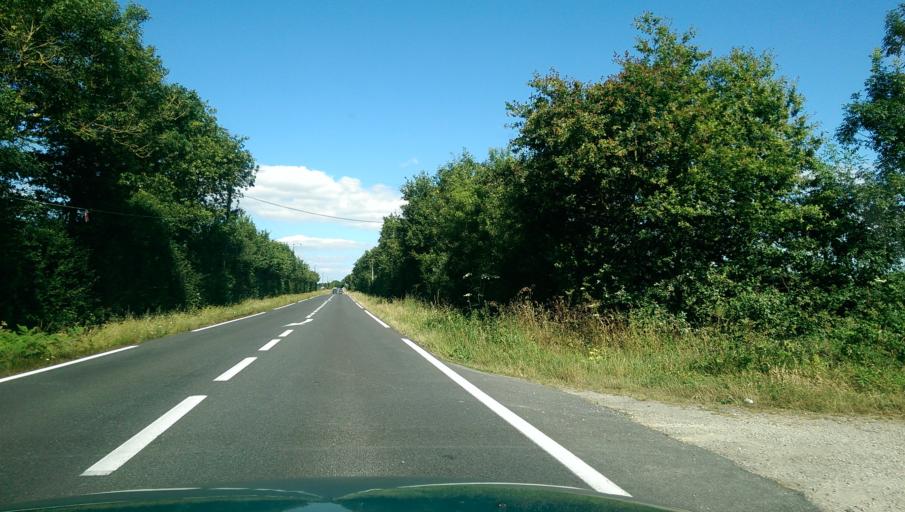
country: FR
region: Pays de la Loire
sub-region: Departement de la Vendee
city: Falleron
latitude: 46.8823
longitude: -1.6946
